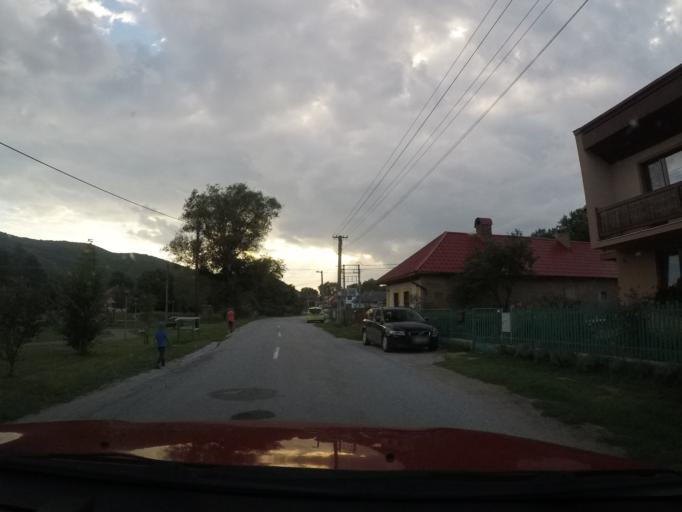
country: SK
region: Kosicky
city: Roznava
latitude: 48.6405
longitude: 20.6541
